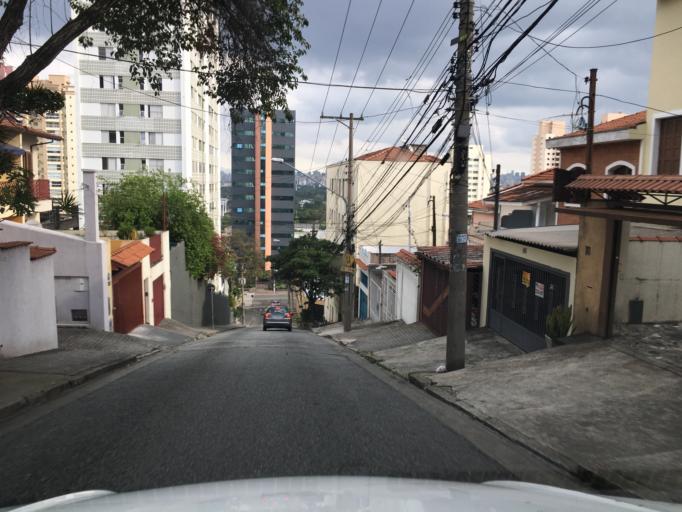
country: BR
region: Sao Paulo
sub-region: Sao Paulo
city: Sao Paulo
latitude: -23.4991
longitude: -46.6286
